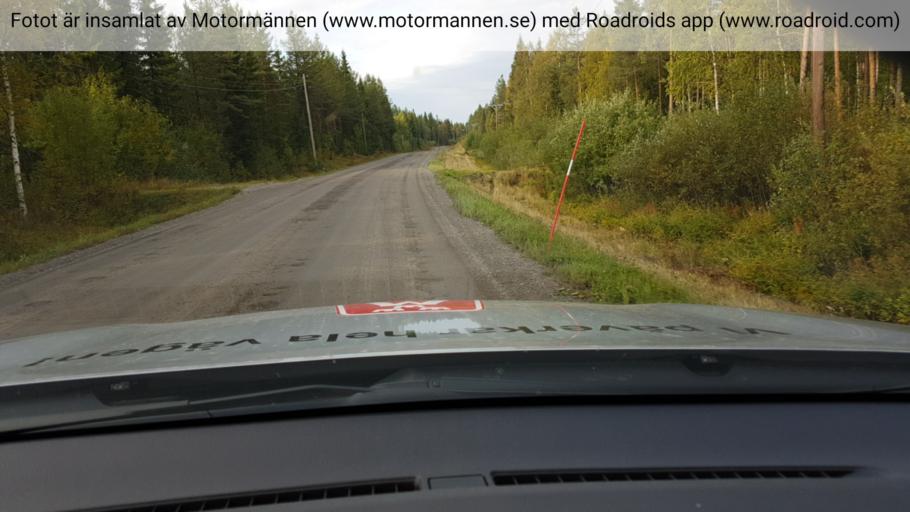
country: SE
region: Jaemtland
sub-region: Stroemsunds Kommun
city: Stroemsund
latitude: 63.9722
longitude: 15.8253
